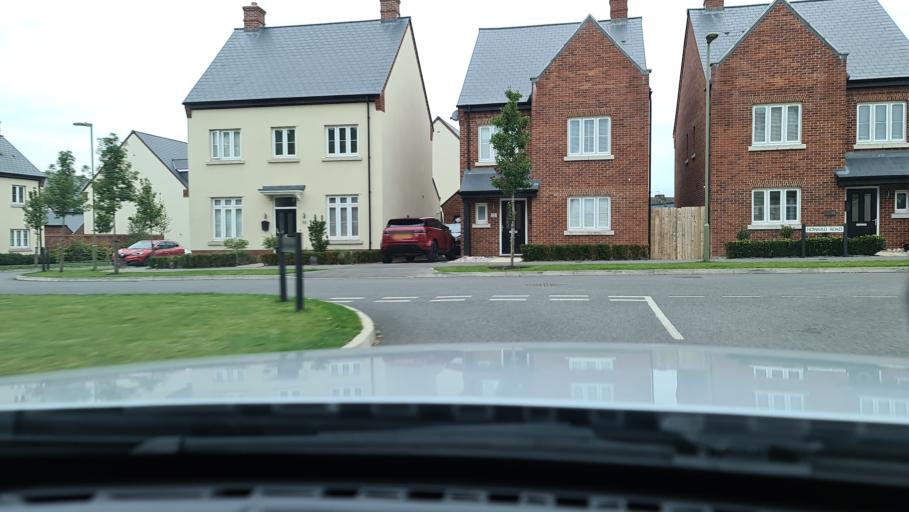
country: GB
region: England
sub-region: Oxfordshire
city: Somerton
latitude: 51.9254
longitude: -1.2551
